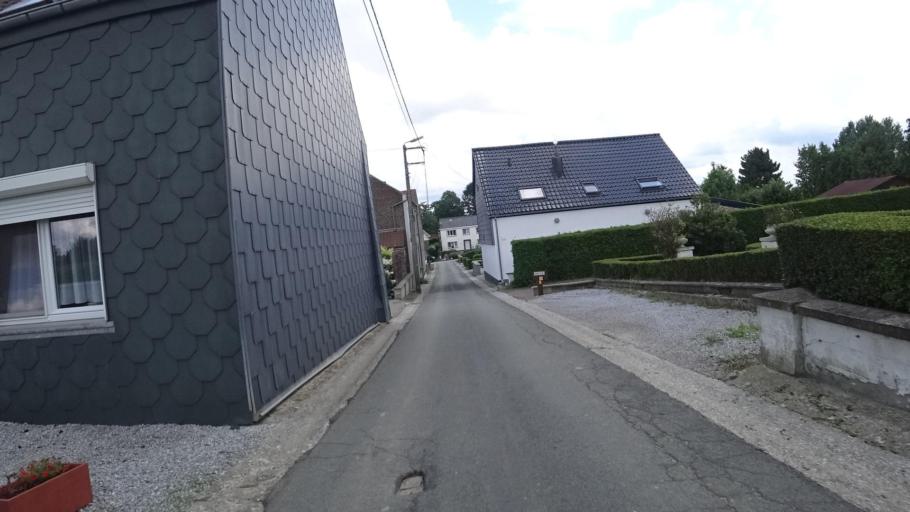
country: BE
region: Wallonia
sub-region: Province du Brabant Wallon
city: Villers-la-Ville
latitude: 50.5468
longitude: 4.5499
